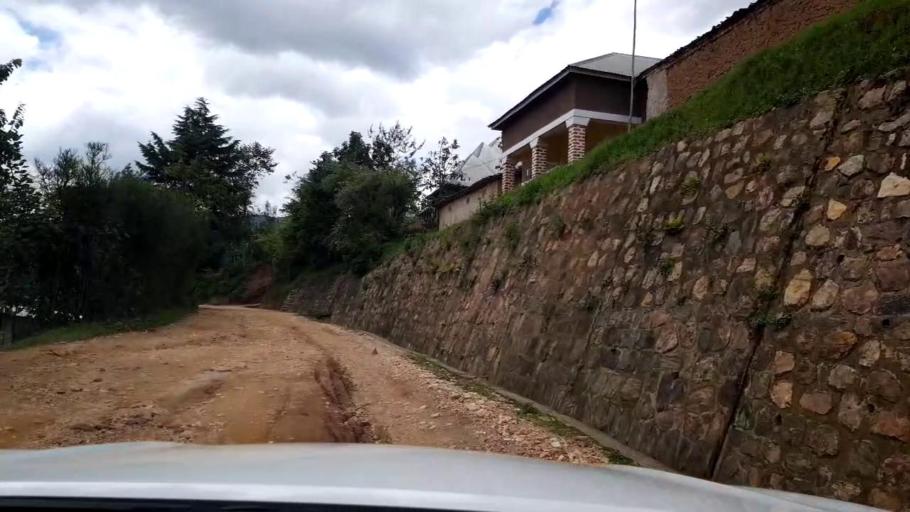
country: RW
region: Southern Province
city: Gitarama
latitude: -1.9390
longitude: 29.6294
